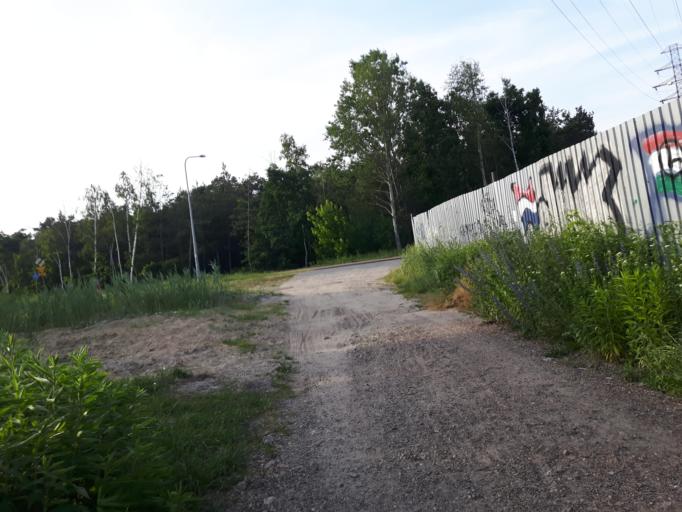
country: PL
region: Masovian Voivodeship
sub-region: Powiat wolominski
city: Zabki
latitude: 52.2870
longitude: 21.1280
